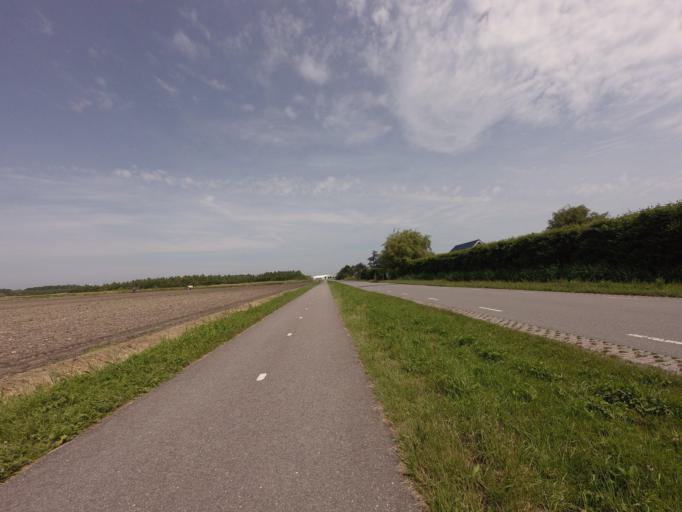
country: NL
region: North Holland
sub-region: Gemeente Enkhuizen
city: Enkhuizen
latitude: 52.7104
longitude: 5.2077
